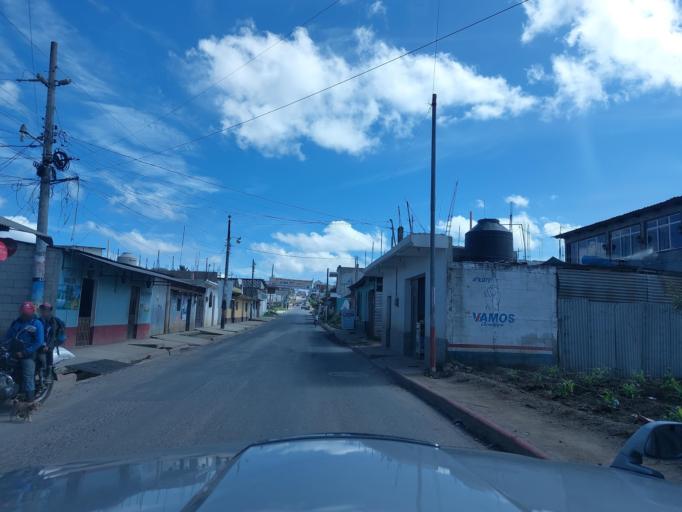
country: GT
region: Chimaltenango
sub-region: Municipio de San Juan Comalapa
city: Comalapa
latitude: 14.7296
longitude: -90.8872
